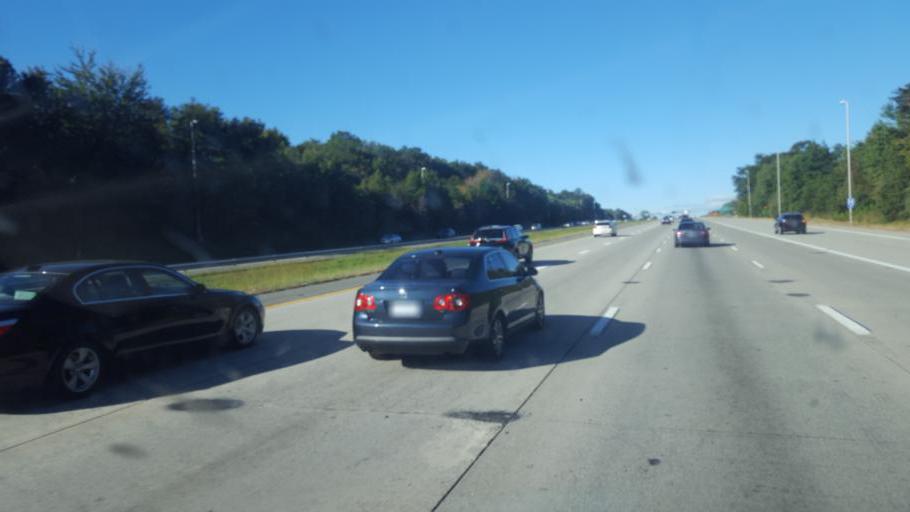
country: US
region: Virginia
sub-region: Fairfax County
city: Greenbriar
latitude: 38.8571
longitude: -77.3751
